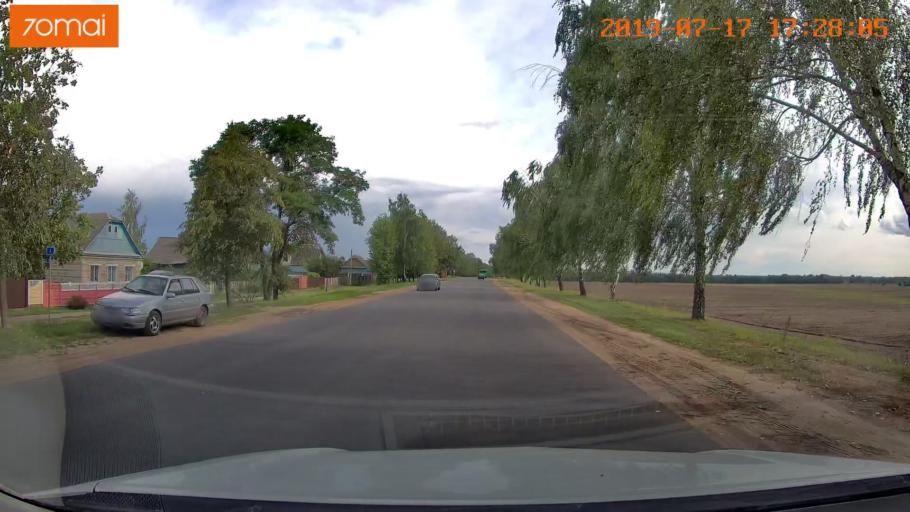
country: BY
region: Mogilev
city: Babruysk
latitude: 53.1325
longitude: 29.1665
